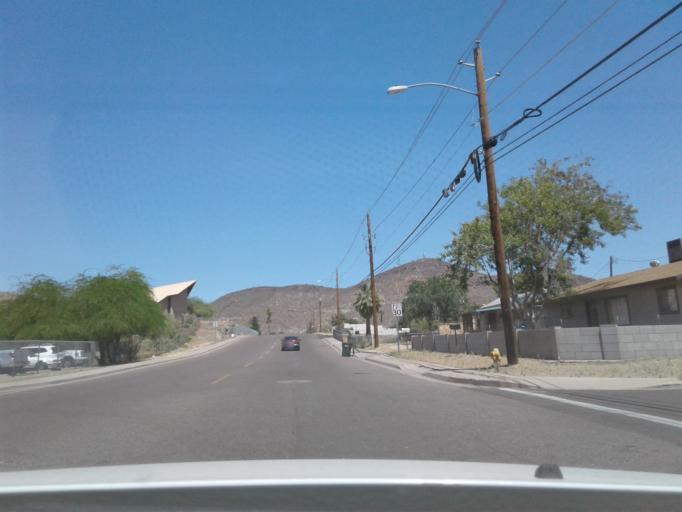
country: US
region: Arizona
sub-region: Maricopa County
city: Glendale
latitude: 33.5758
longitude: -112.0912
